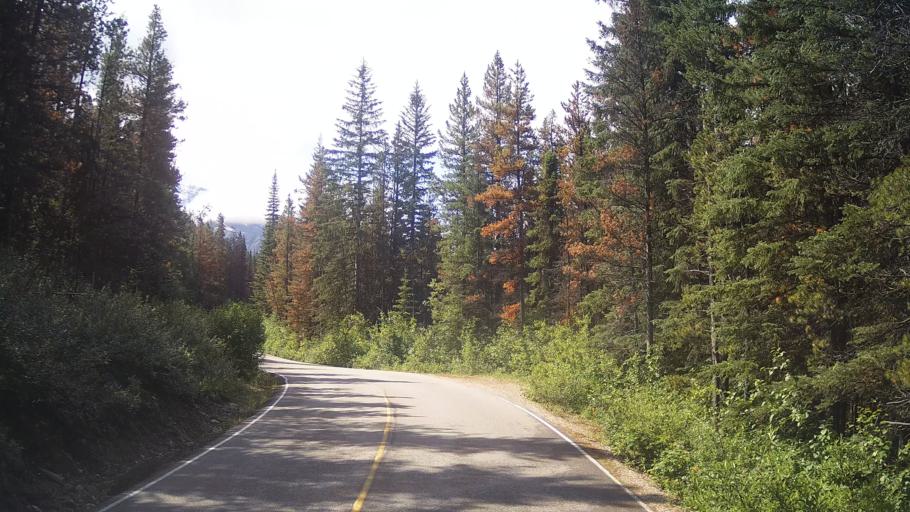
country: CA
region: Alberta
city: Jasper Park Lodge
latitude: 52.7528
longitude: -118.0448
